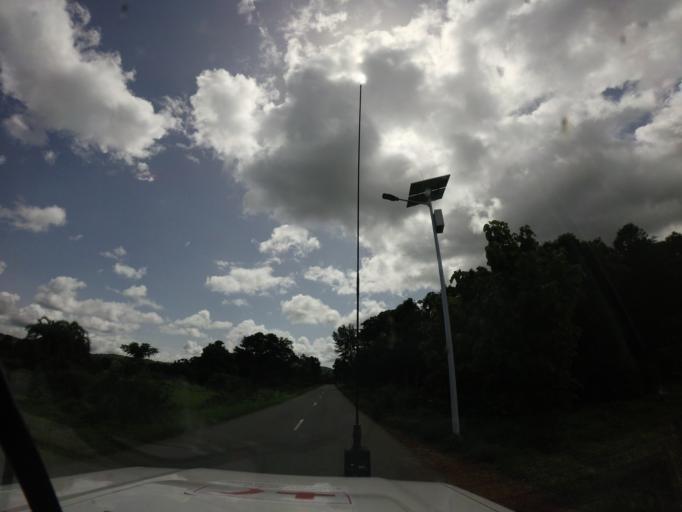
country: GN
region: Mamou
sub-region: Mamou Prefecture
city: Mamou
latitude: 10.2890
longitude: -11.9779
